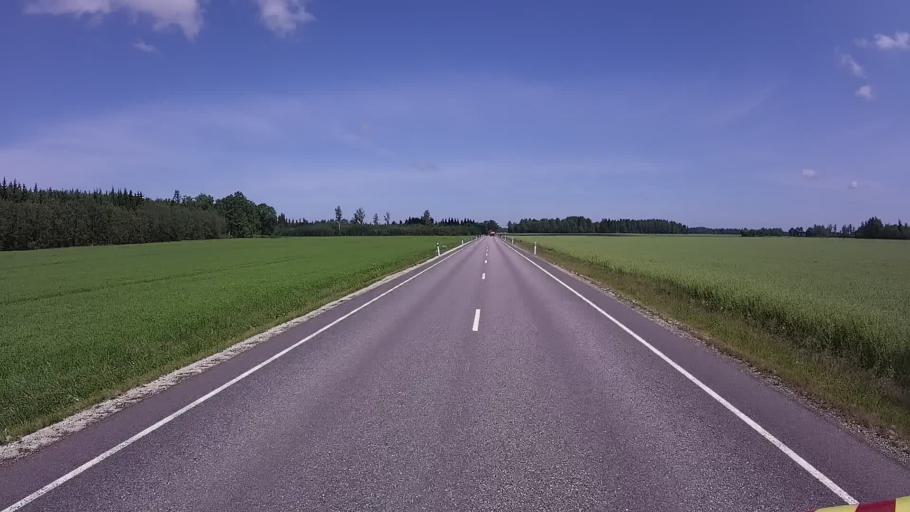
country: EE
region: Tartu
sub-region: Tartu linn
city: Tartu
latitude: 58.3845
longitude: 26.8881
